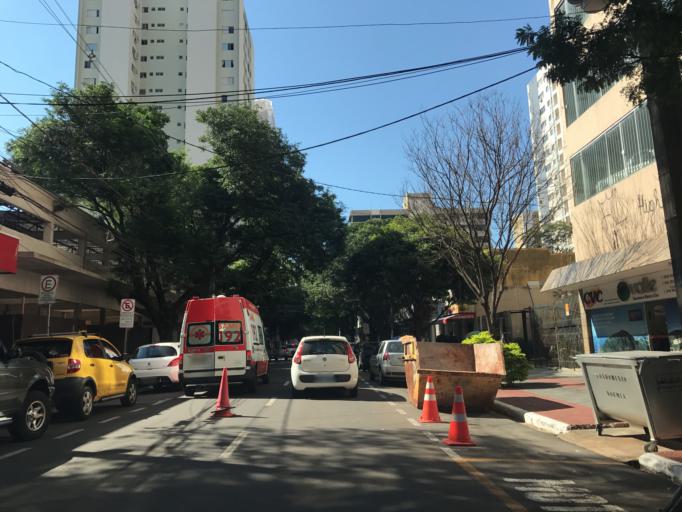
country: BR
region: Parana
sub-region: Maringa
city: Maringa
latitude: -23.4227
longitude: -51.9424
